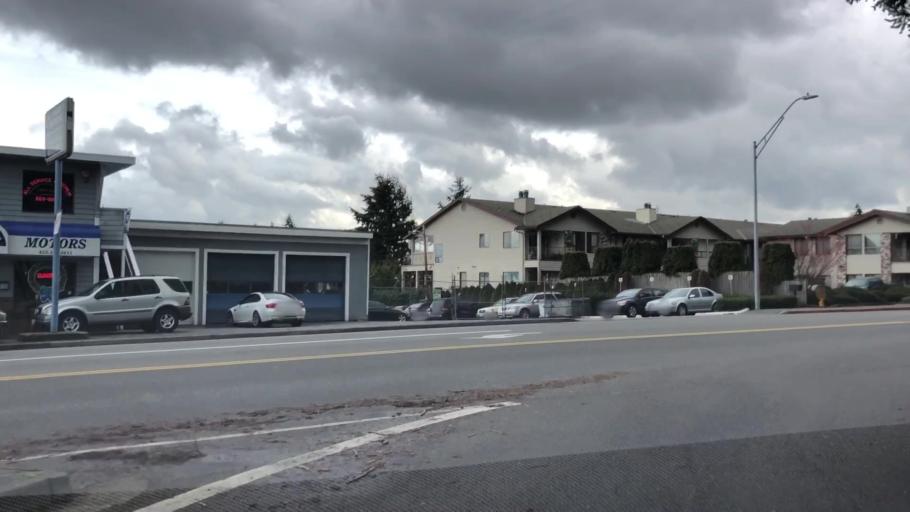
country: US
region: Washington
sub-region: Snohomish County
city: Everett
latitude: 47.9494
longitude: -122.2067
